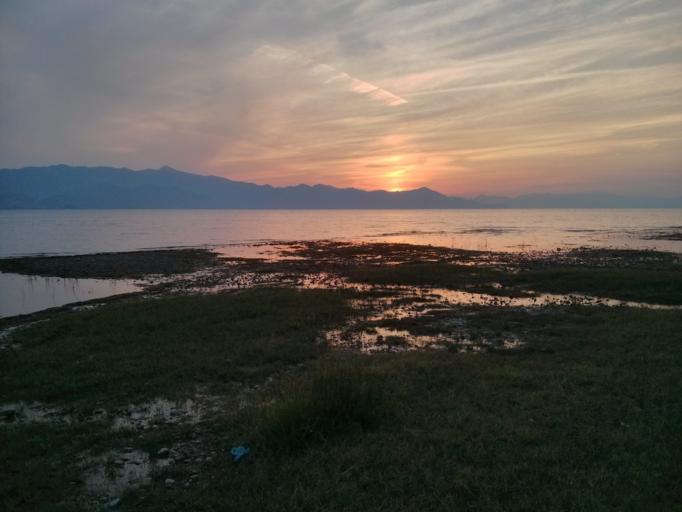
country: AL
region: Shkoder
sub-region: Rrethi i Malesia e Madhe
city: Grude-Fushe
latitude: 42.1382
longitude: 19.4646
